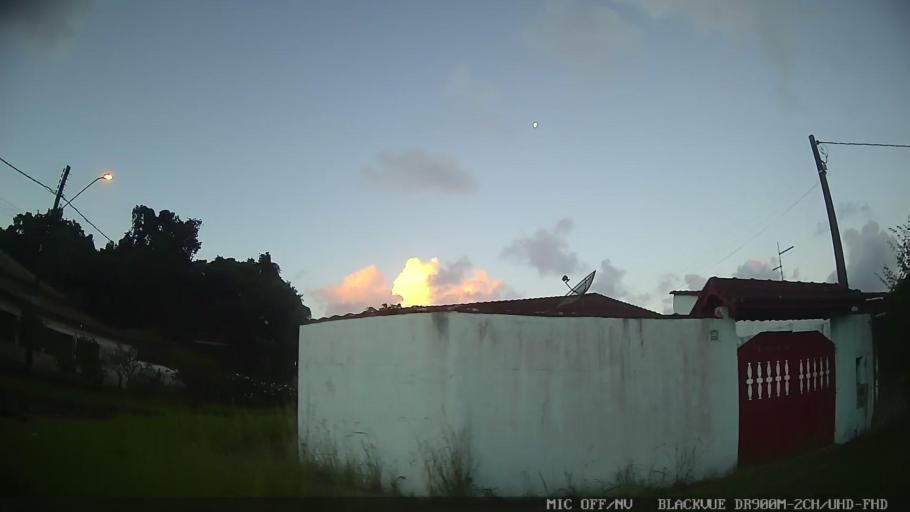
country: BR
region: Sao Paulo
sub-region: Itanhaem
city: Itanhaem
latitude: -24.1480
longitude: -46.7382
